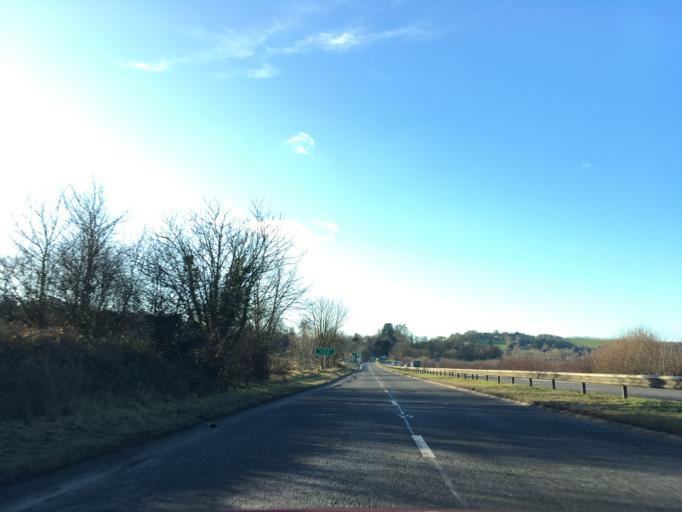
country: GB
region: England
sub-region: Bath and North East Somerset
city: Corston
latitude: 51.3871
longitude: -2.4229
